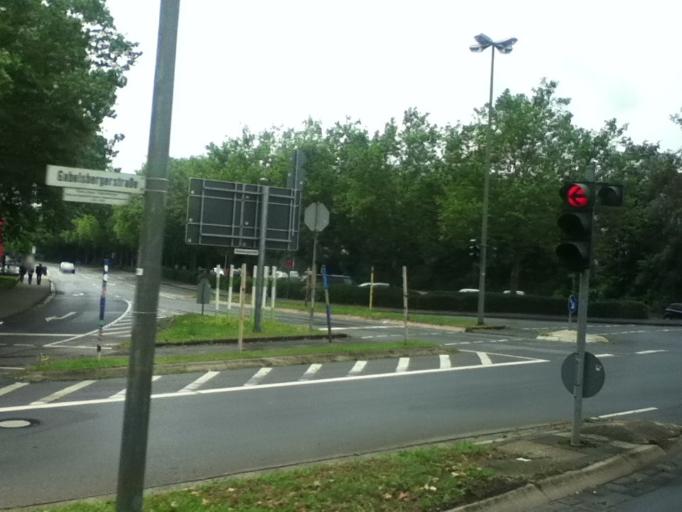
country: DE
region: Hesse
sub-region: Regierungsbezirk Giessen
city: Giessen
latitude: 50.5854
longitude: 8.6653
